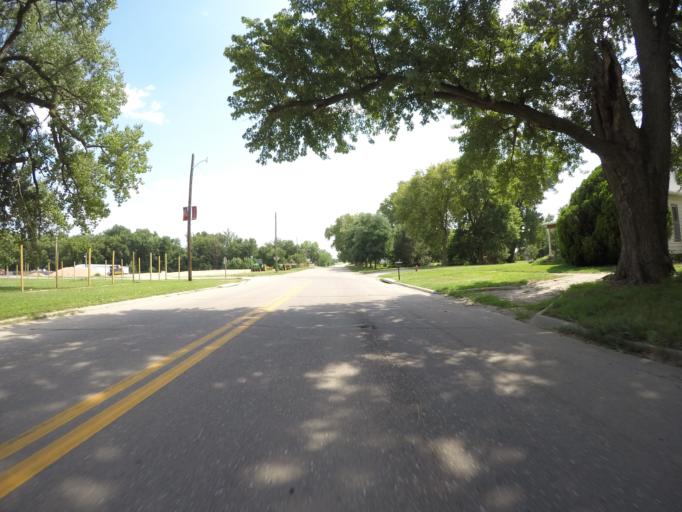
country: US
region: Nebraska
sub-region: Nuckolls County
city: Nelson
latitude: 40.1988
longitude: -98.0673
